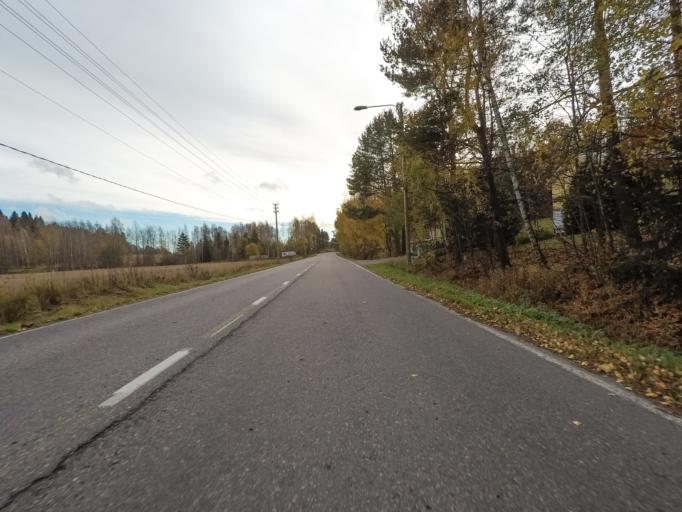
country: FI
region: Uusimaa
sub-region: Helsinki
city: Vantaa
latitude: 60.2661
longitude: 25.1394
